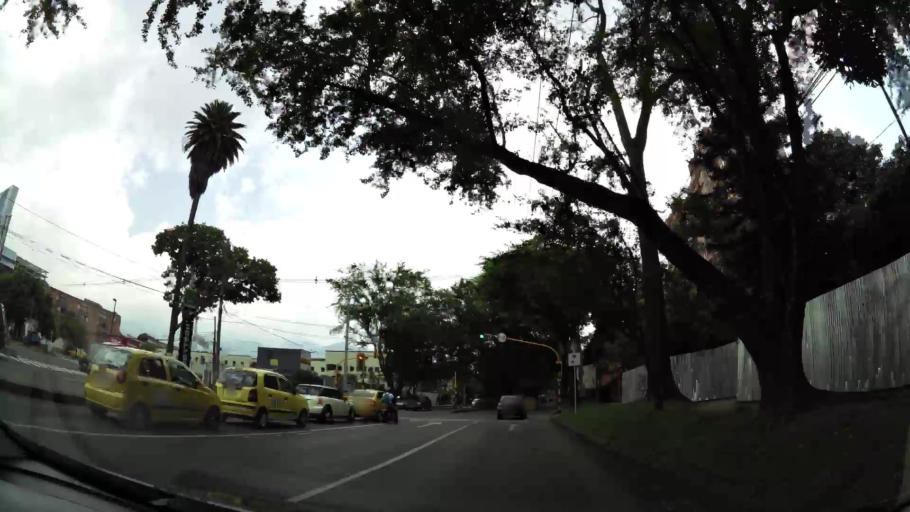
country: CO
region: Antioquia
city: Envigado
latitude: 6.1793
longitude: -75.5836
